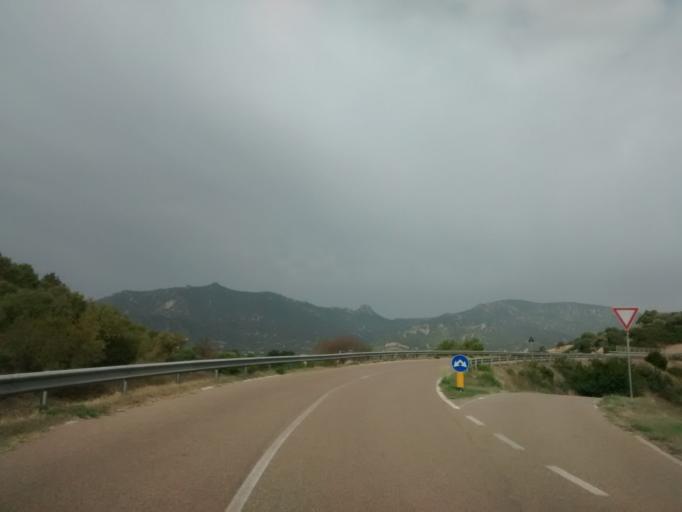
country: IT
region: Sardinia
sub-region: Provincia di Cagliari
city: Villasimius
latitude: 39.1445
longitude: 9.5267
